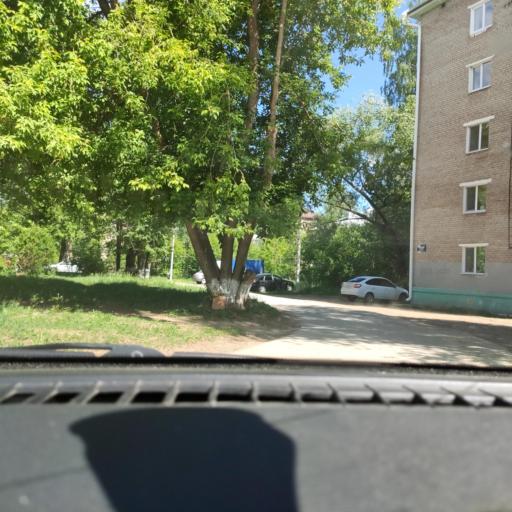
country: RU
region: Perm
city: Krasnokamsk
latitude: 58.0883
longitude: 55.7534
